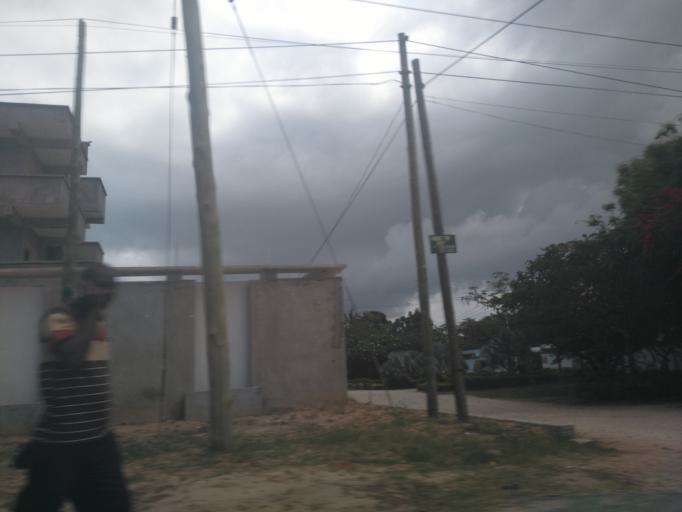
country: TZ
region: Dar es Salaam
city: Magomeni
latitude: -6.7556
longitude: 39.2771
